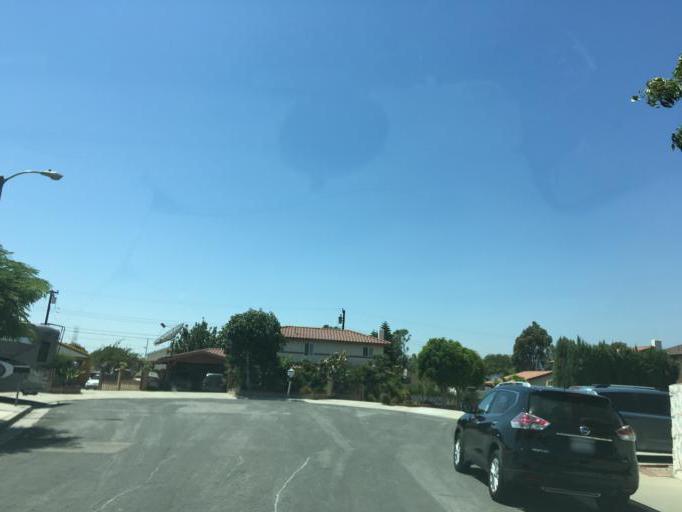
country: US
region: California
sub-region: Los Angeles County
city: Avocado Heights
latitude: 34.0443
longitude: -118.0014
